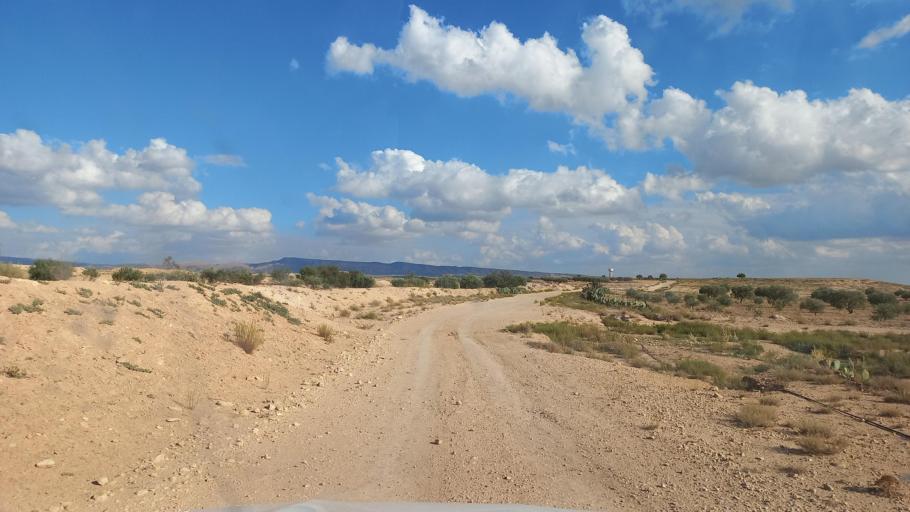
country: TN
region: Al Qasrayn
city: Sbiba
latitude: 35.3972
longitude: 9.0380
